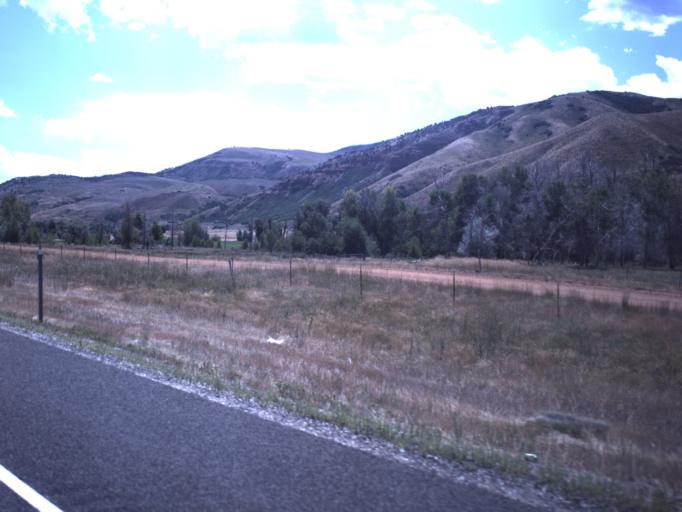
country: US
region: Utah
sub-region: Summit County
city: Coalville
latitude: 40.9904
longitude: -111.4564
